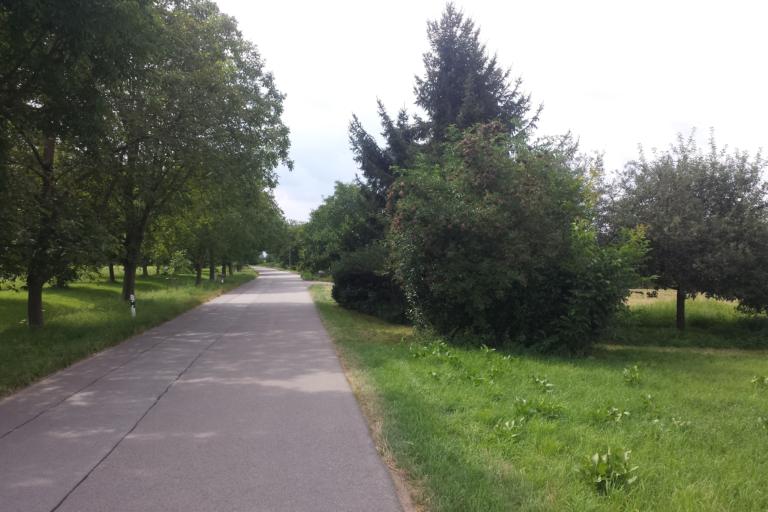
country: DE
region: Baden-Wuerttemberg
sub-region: Karlsruhe Region
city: Weinheim
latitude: 49.5595
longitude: 8.6386
